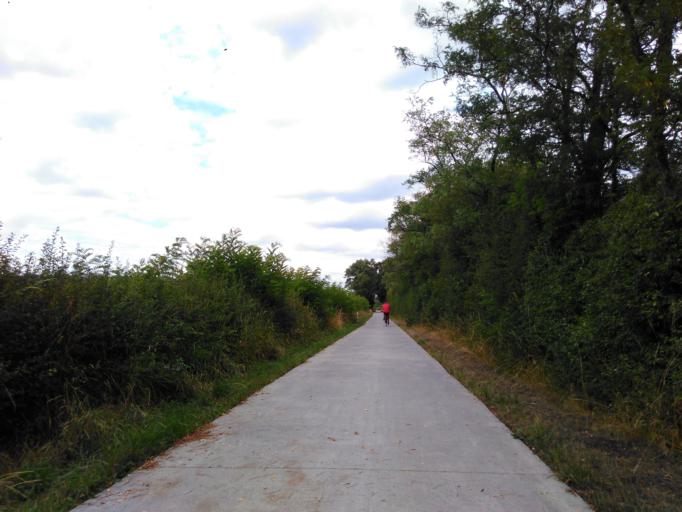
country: LU
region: Grevenmacher
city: Gonderange
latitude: 49.6844
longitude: 6.2501
